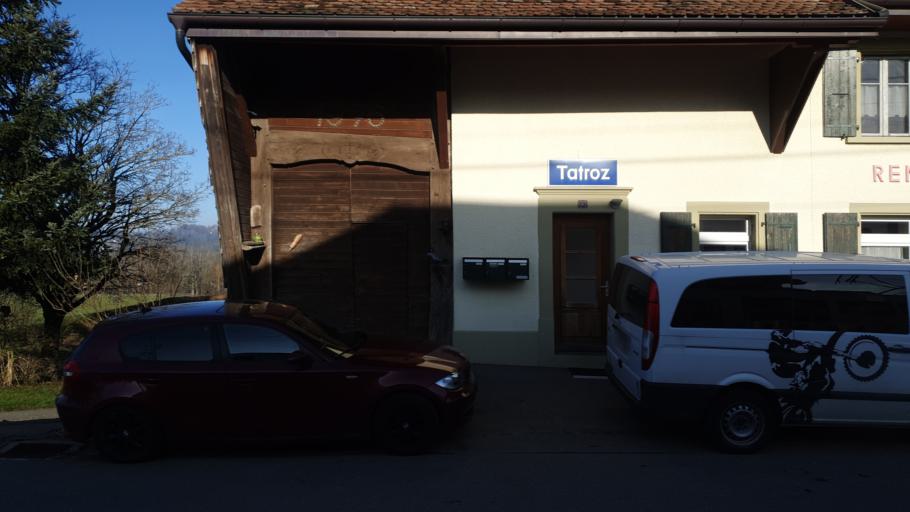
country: CH
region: Fribourg
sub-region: Veveyse District
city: Attalens
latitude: 46.5233
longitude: 6.8633
